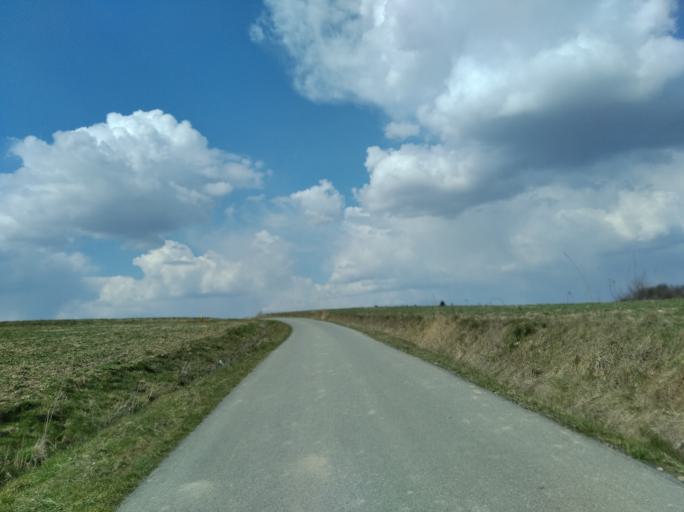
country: PL
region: Subcarpathian Voivodeship
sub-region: Powiat strzyzowski
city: Wisniowa
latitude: 49.9356
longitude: 21.7189
